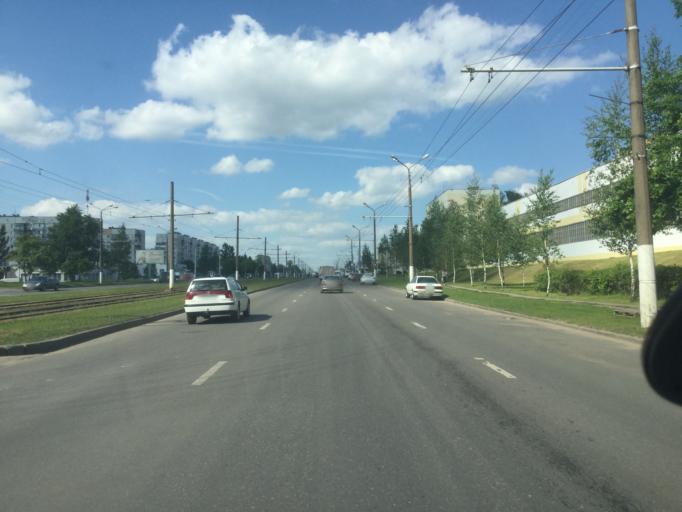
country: BY
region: Vitebsk
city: Vitebsk
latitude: 55.1701
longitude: 30.2426
